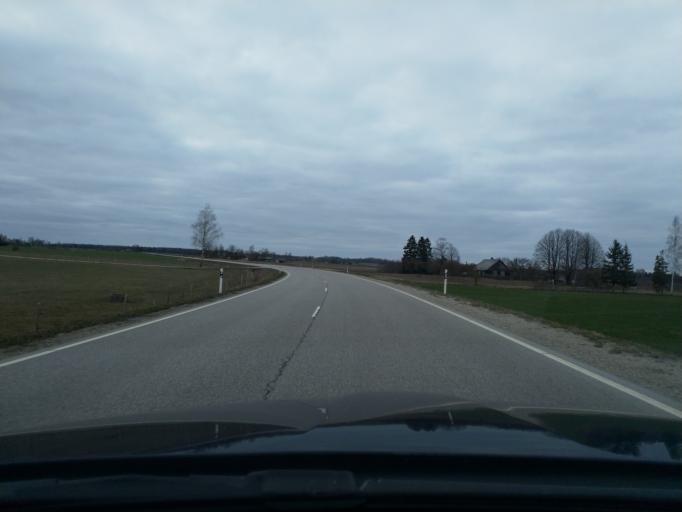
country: LV
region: Talsu Rajons
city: Sabile
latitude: 56.9351
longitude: 22.5144
